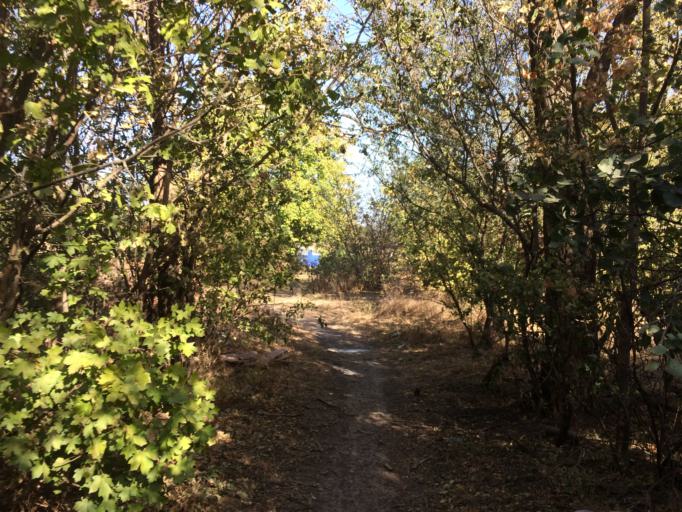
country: RU
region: Rostov
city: Tselina
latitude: 46.5145
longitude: 41.1830
